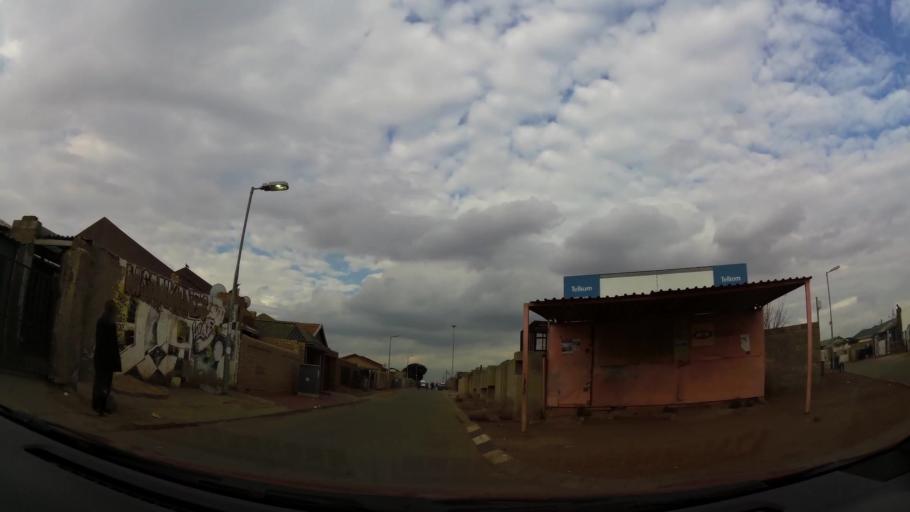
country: ZA
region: Gauteng
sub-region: City of Johannesburg Metropolitan Municipality
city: Soweto
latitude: -26.2512
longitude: 27.8252
